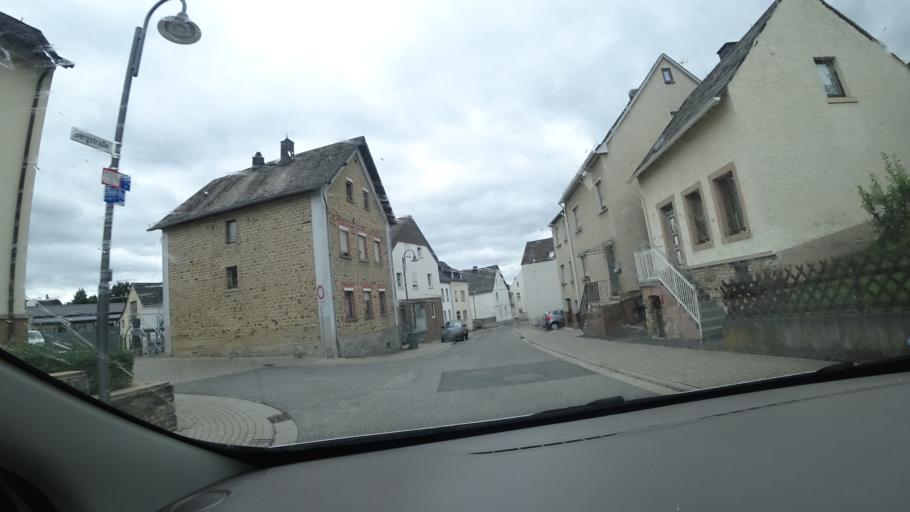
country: DE
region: Rheinland-Pfalz
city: Hohr-Grenzhausen
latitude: 50.4322
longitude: 7.6778
